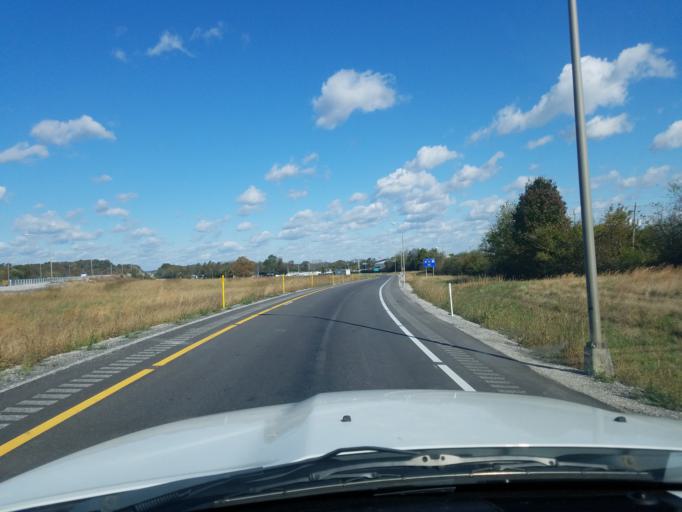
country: US
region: Kentucky
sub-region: Warren County
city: Bowling Green
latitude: 36.9544
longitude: -86.4962
